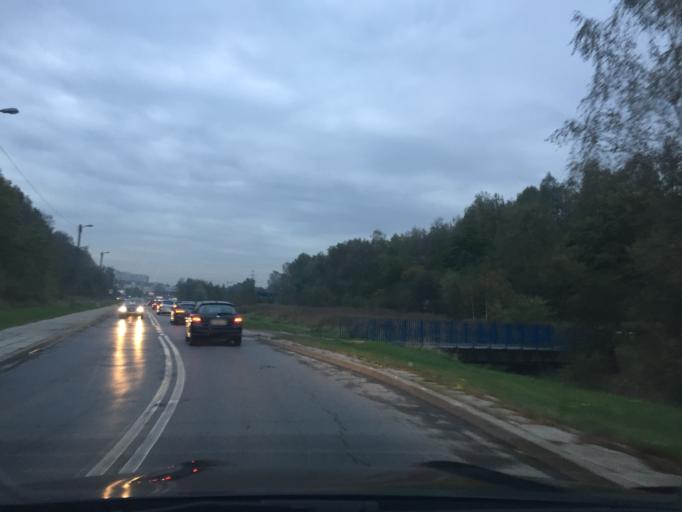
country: PL
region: Lesser Poland Voivodeship
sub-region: Powiat krakowski
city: Wrzasowice
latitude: 50.0055
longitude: 19.9379
